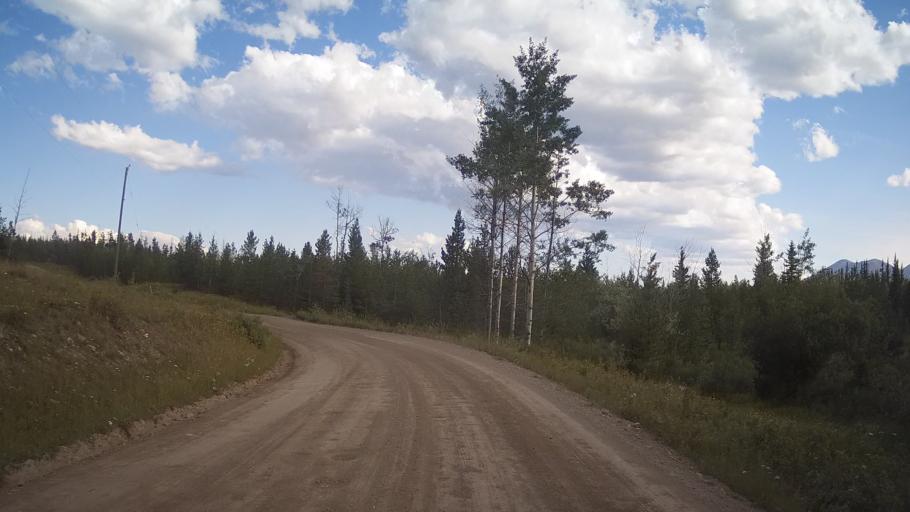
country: CA
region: British Columbia
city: Lillooet
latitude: 51.2846
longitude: -121.7471
